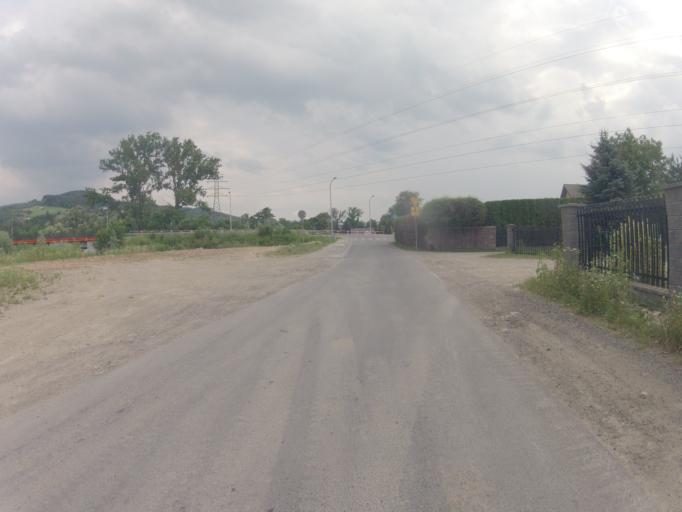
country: PL
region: Lesser Poland Voivodeship
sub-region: Powiat nowosadecki
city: Stary Sacz
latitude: 49.5429
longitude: 20.6551
